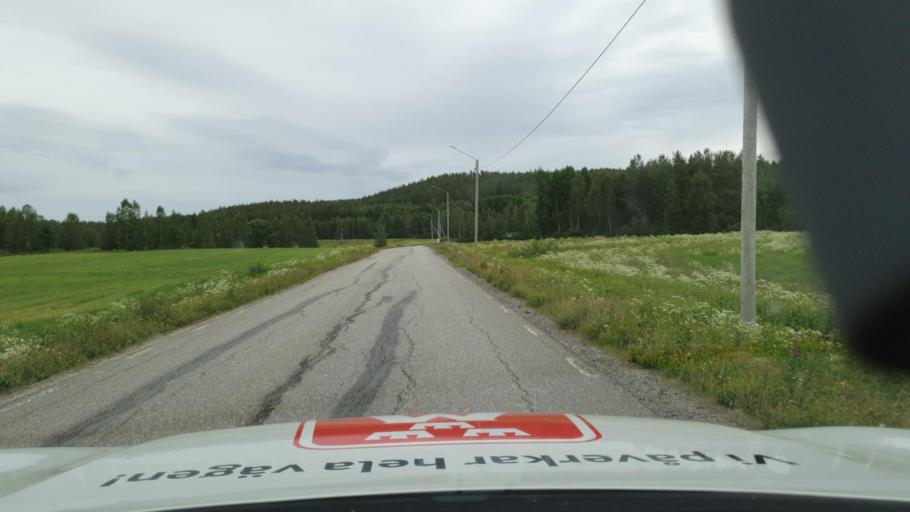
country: SE
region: Vaesterbotten
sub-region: Skelleftea Kommun
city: Burtraesk
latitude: 64.3083
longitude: 20.6540
